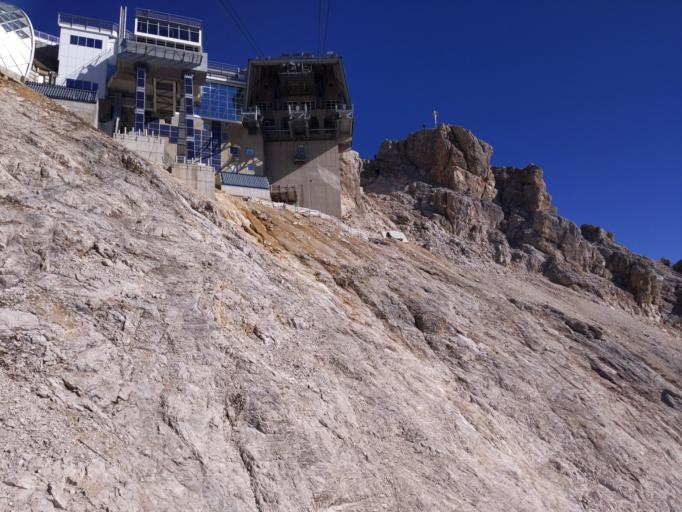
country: DE
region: Bavaria
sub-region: Upper Bavaria
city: Grainau
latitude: 47.4203
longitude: 10.9852
